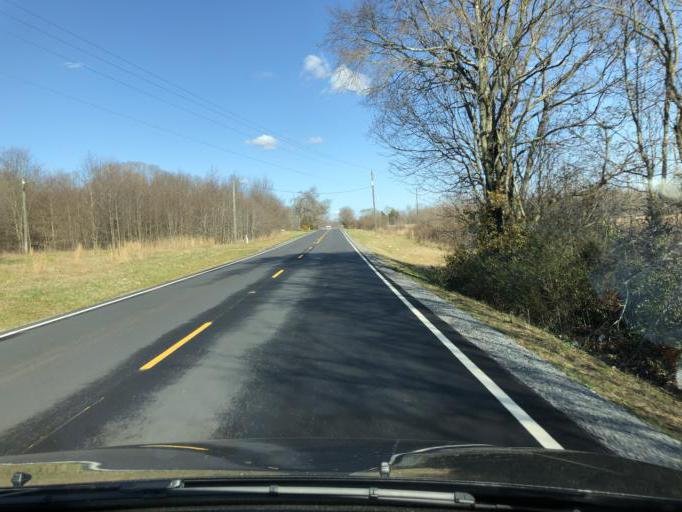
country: US
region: North Carolina
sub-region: Cleveland County
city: Shelby
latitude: 35.2078
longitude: -81.5451
